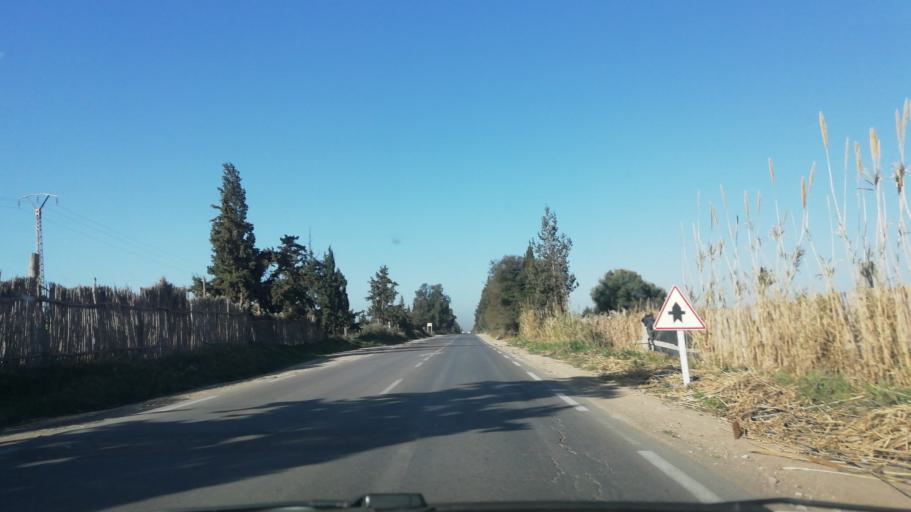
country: DZ
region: Mascara
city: Sig
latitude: 35.5718
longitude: -0.0283
